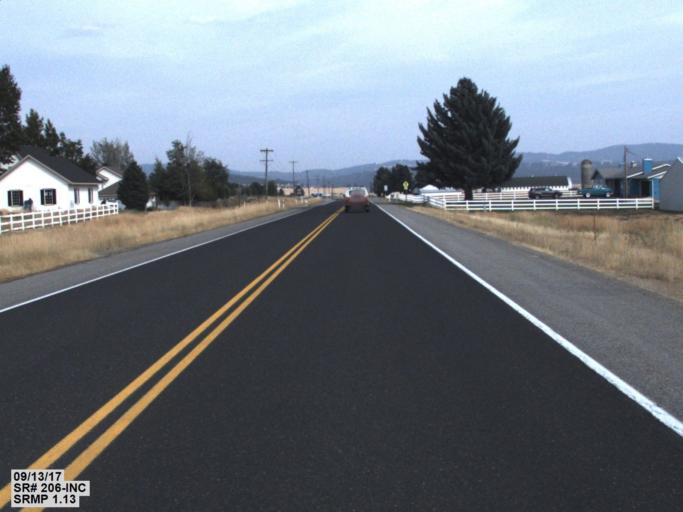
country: US
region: Washington
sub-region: Spokane County
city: Mead
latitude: 47.7873
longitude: -117.3306
